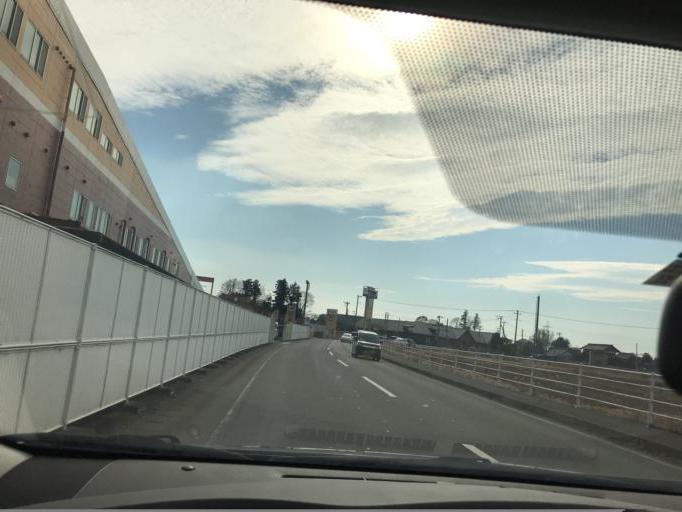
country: JP
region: Ibaraki
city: Naka
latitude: 36.0765
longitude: 140.0700
